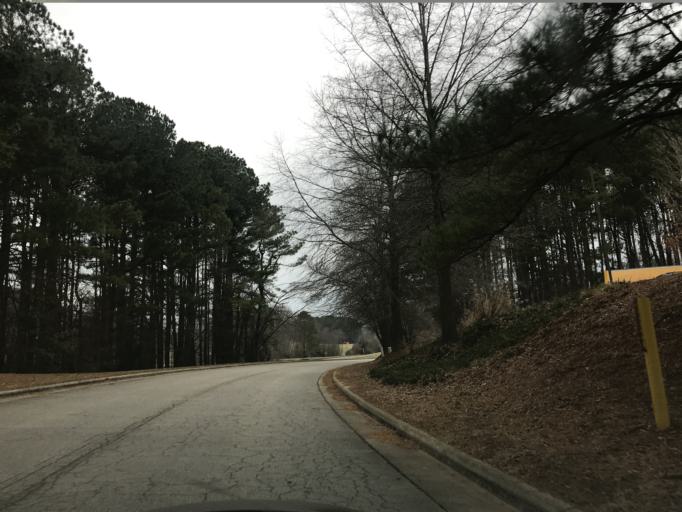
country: US
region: North Carolina
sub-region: Wake County
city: Raleigh
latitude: 35.7641
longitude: -78.6592
